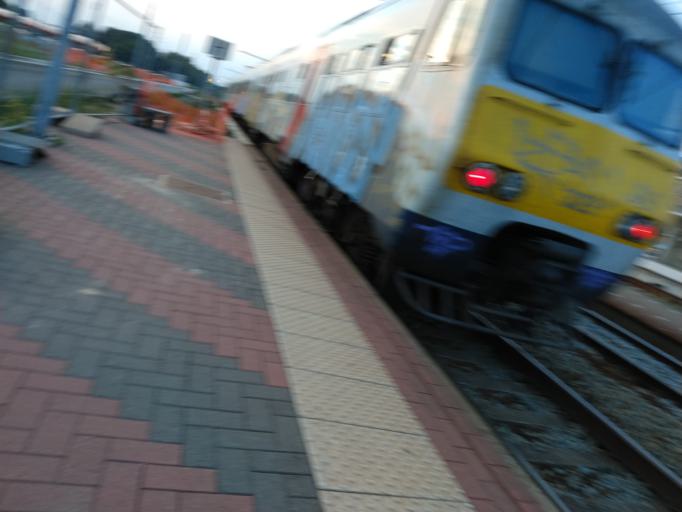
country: BE
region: Flanders
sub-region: Provincie Vlaams-Brabant
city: Tienen
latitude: 50.8068
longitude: 4.9270
